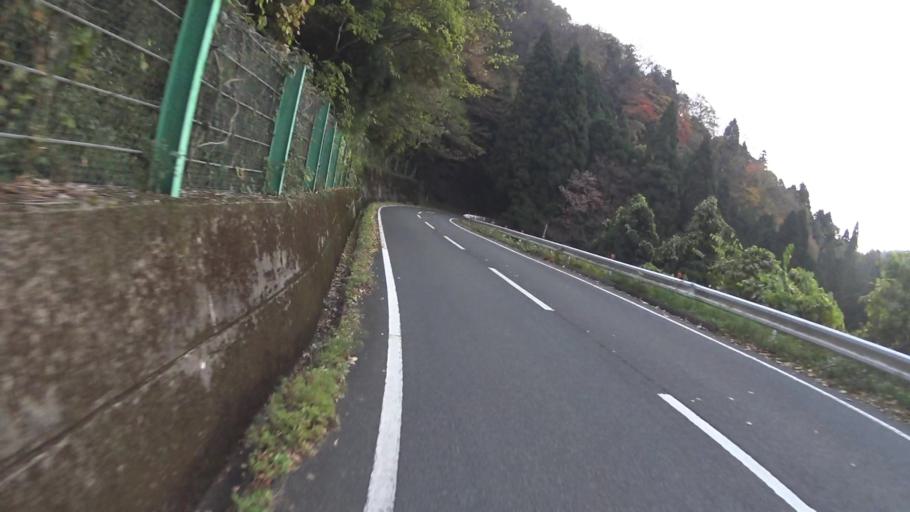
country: JP
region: Kyoto
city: Maizuru
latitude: 35.5398
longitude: 135.4501
